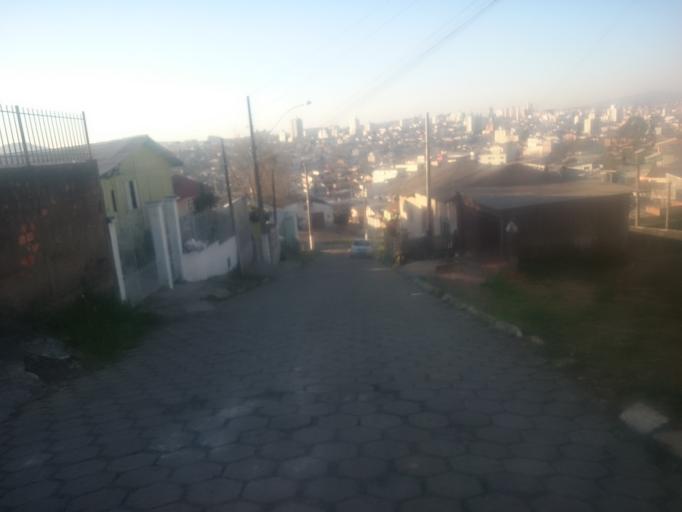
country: BR
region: Santa Catarina
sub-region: Lages
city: Lages
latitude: -27.8325
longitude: -50.3310
